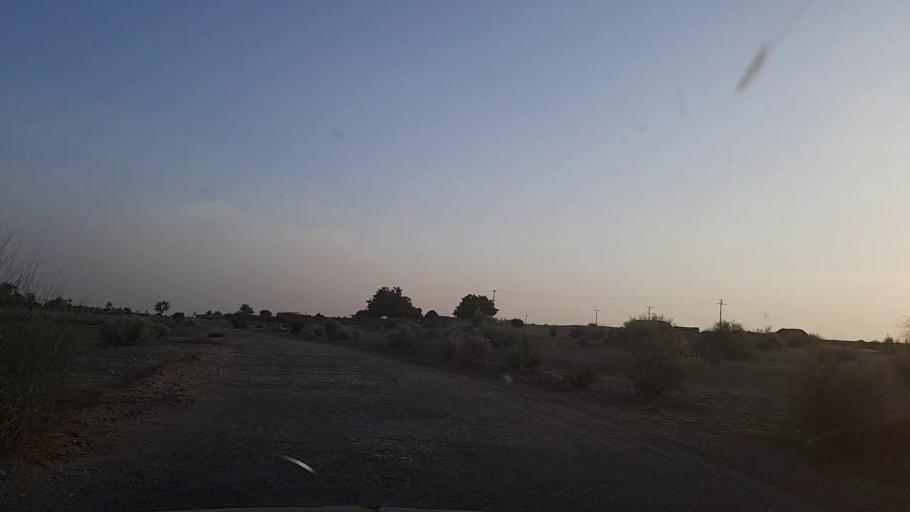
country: PK
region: Sindh
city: Khanpur
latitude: 27.5982
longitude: 69.4272
